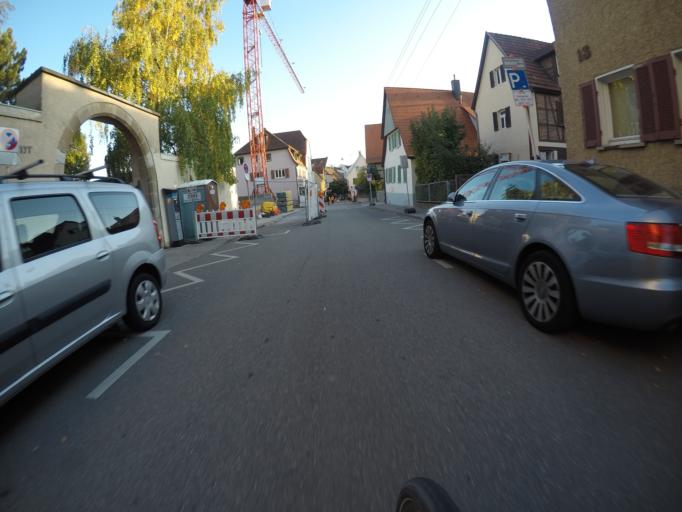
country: DE
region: Baden-Wuerttemberg
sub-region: Regierungsbezirk Stuttgart
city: Steinenbronn
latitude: 48.7323
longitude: 9.1097
